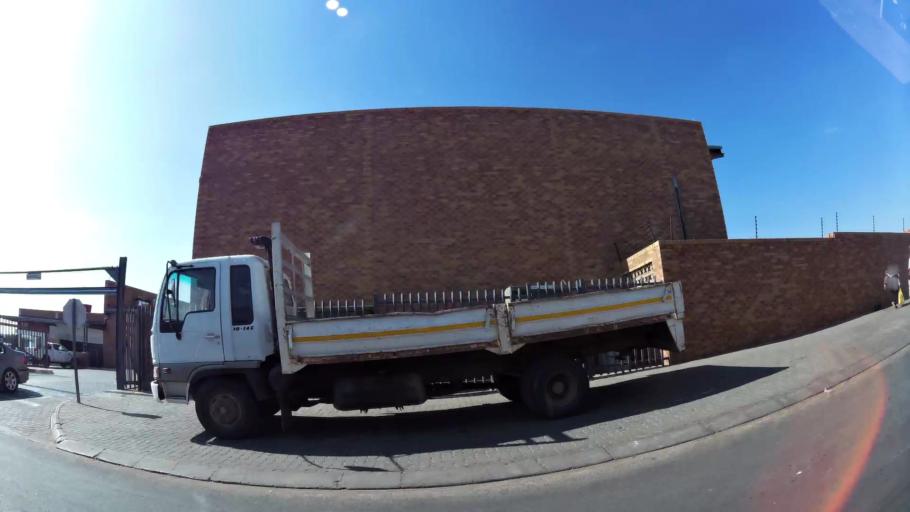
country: ZA
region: Gauteng
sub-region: West Rand District Municipality
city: Muldersdriseloop
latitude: -26.0182
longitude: 27.9383
